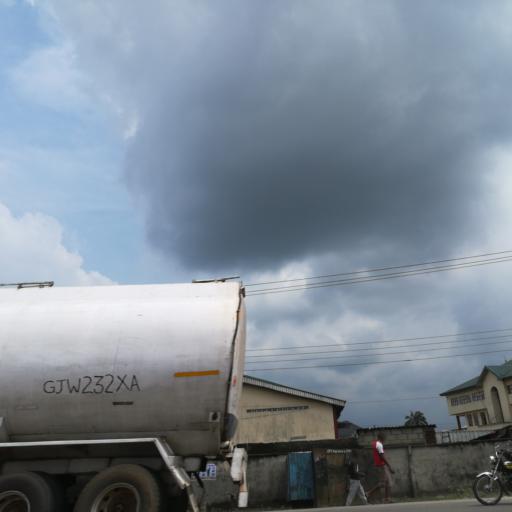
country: NG
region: Rivers
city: Port Harcourt
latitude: 4.8489
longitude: 7.0736
